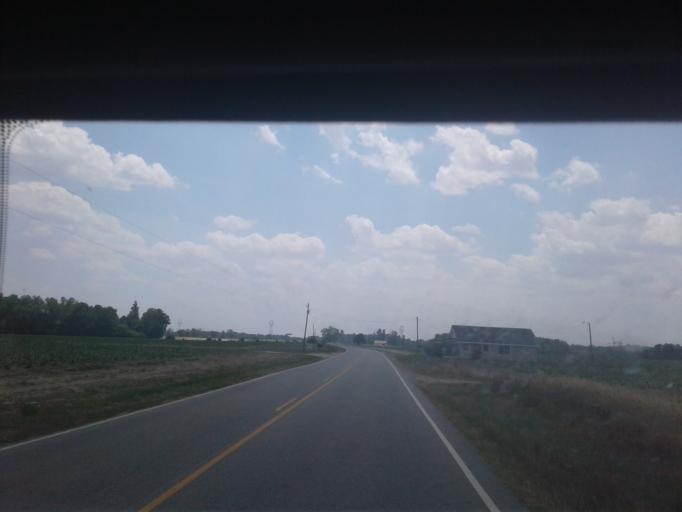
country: US
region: North Carolina
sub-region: Harnett County
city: Erwin
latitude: 35.3610
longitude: -78.6356
